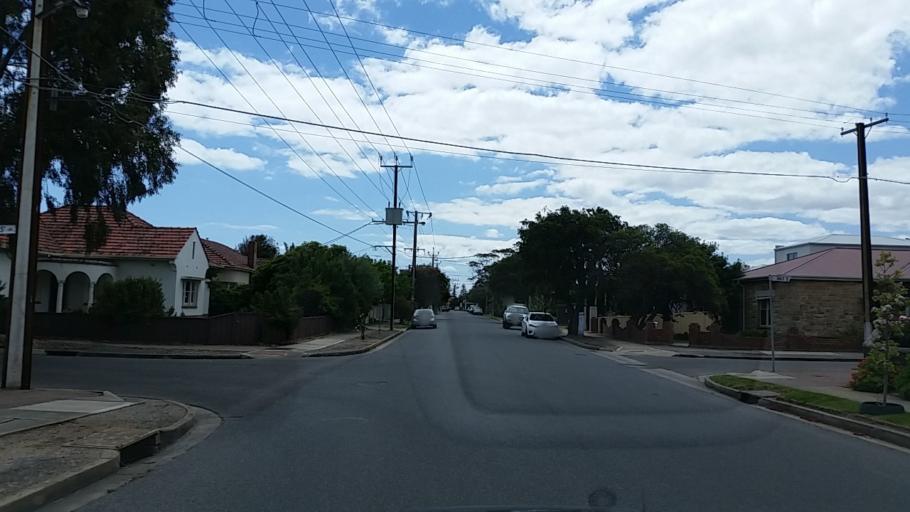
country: AU
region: South Australia
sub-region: Holdfast Bay
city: North Brighton
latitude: -34.9935
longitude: 138.5161
